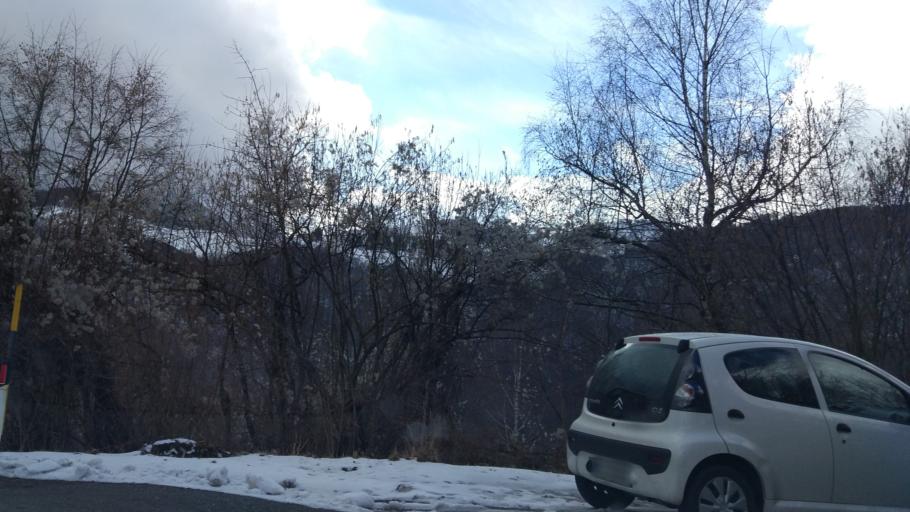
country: IT
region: Lombardy
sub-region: Provincia di Lecco
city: Moggio
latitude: 45.9141
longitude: 9.4963
